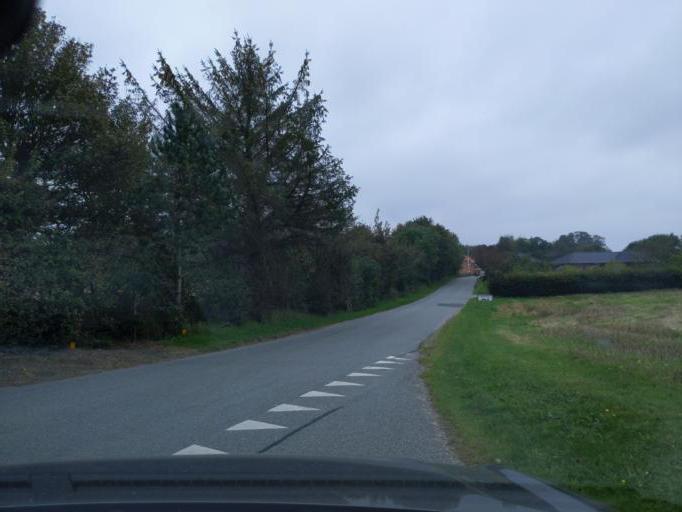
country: DK
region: Central Jutland
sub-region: Viborg Kommune
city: Viborg
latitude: 56.4847
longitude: 9.3052
